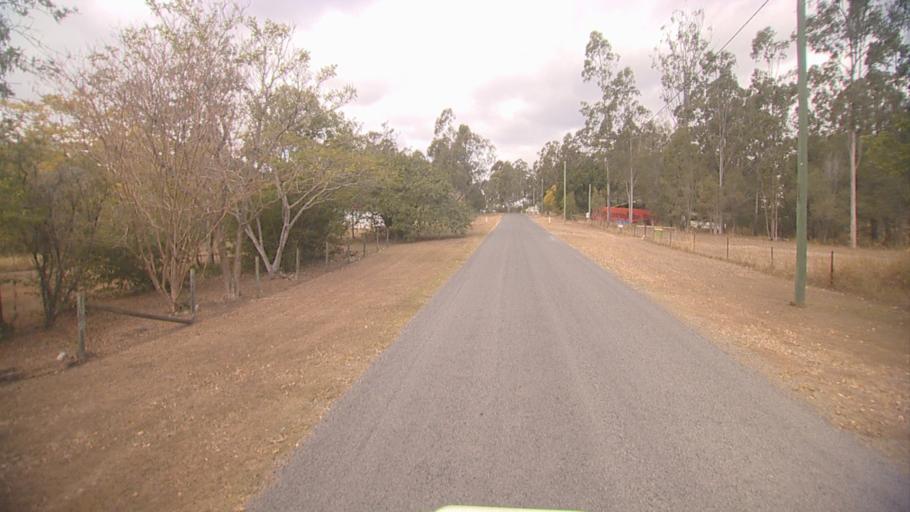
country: AU
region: Queensland
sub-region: Logan
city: Cedar Vale
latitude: -27.8787
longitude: 153.0138
